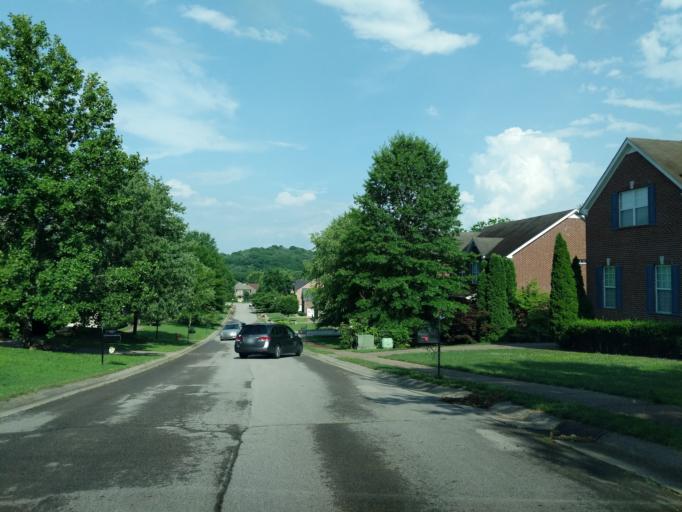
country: US
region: Tennessee
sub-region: Cheatham County
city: Pegram
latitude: 36.0387
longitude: -86.9603
